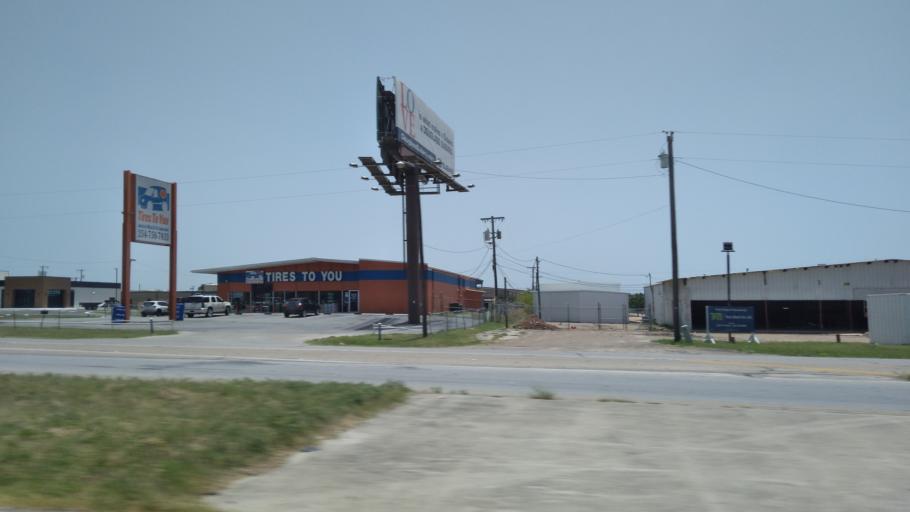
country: US
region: Texas
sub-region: McLennan County
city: Woodway
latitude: 31.5106
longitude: -97.1921
